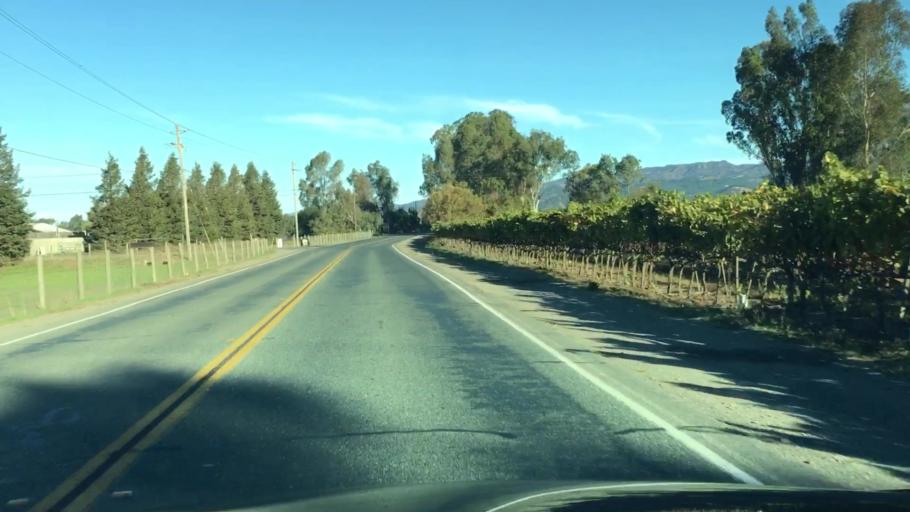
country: US
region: California
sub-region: Sonoma County
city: Sonoma
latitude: 38.2481
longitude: -122.4399
